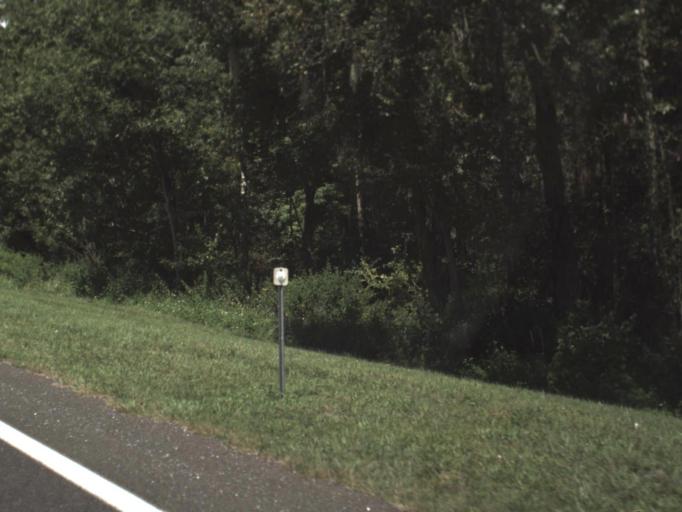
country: US
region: Florida
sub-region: Polk County
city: Fussels Corner
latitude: 28.0480
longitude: -81.8742
